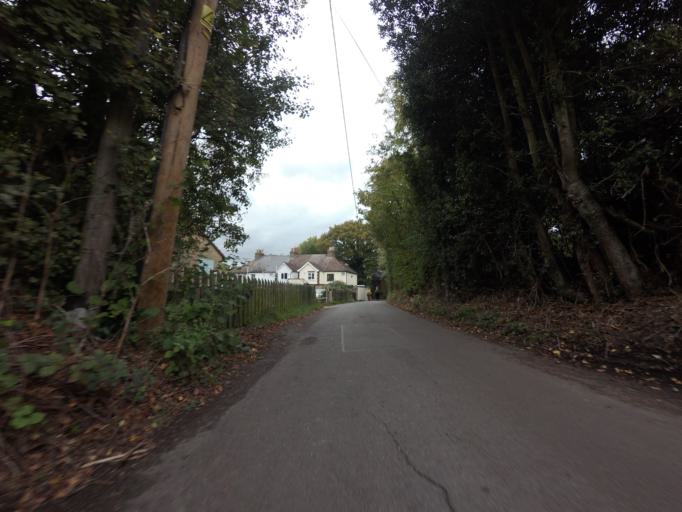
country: GB
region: England
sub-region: Kent
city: Swanley
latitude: 51.3866
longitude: 0.1598
